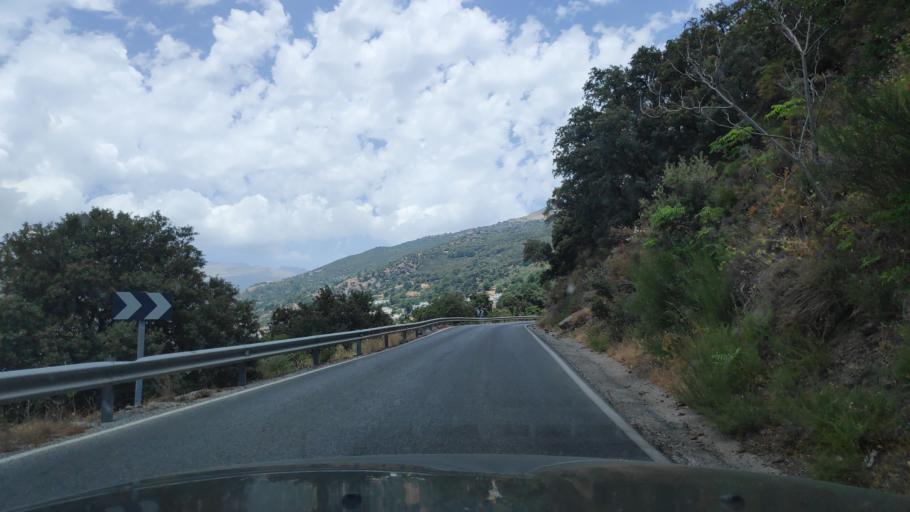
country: ES
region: Andalusia
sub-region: Provincia de Granada
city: Pampaneira
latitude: 36.9395
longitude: -3.3570
